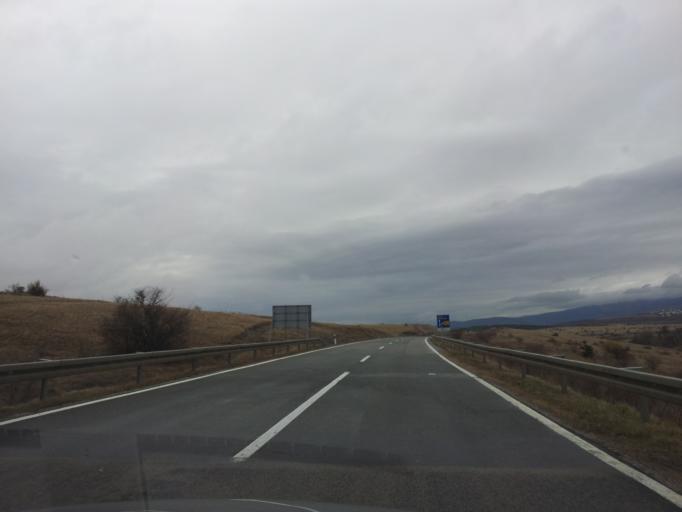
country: HR
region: Zadarska
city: Gracac
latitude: 44.4978
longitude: 15.7466
